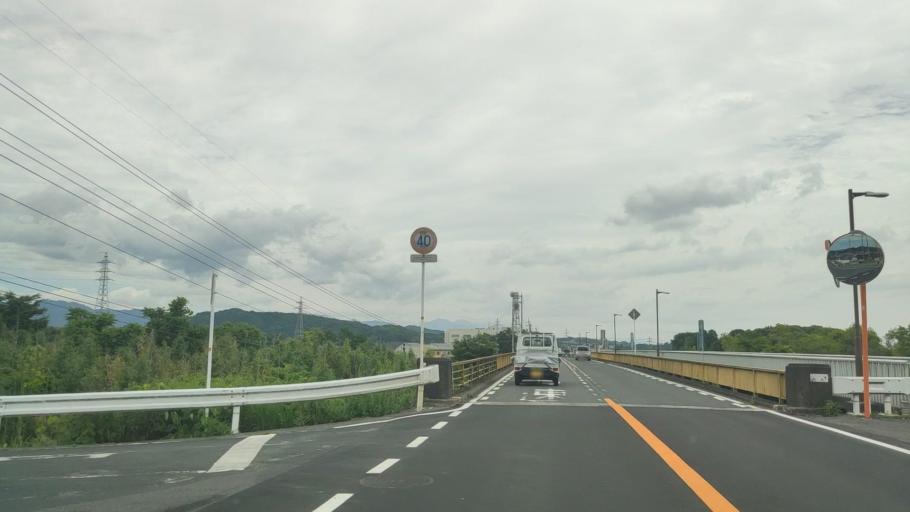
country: JP
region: Okayama
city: Tsuyama
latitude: 35.0563
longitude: 133.9380
